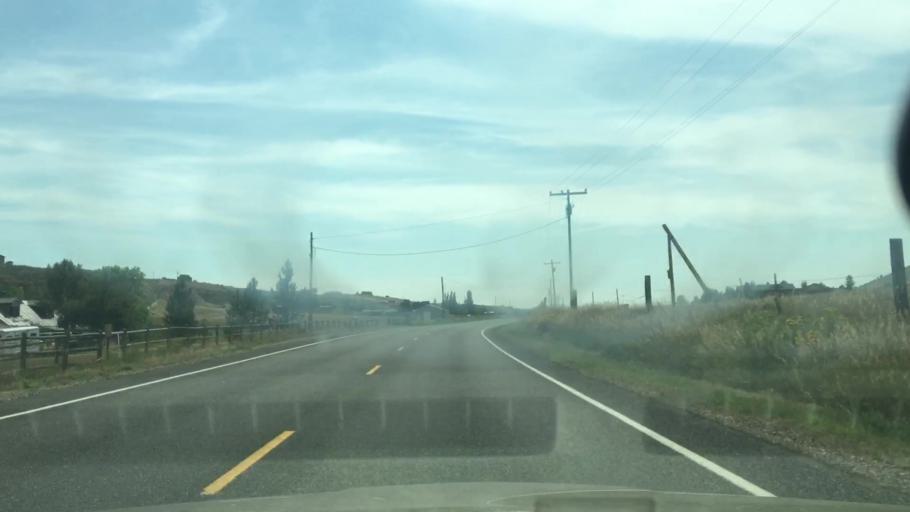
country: US
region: Colorado
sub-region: Larimer County
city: Campion
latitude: 40.3579
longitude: -105.1856
